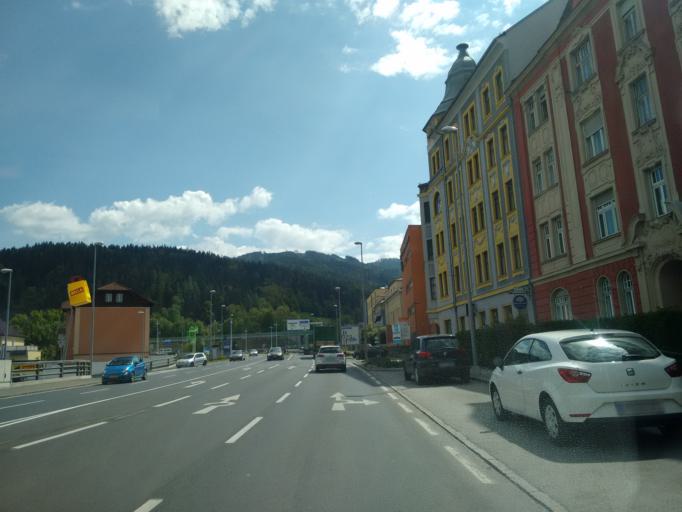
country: AT
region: Styria
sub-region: Politischer Bezirk Bruck-Muerzzuschlag
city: Bruck an der Mur
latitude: 47.4087
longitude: 15.2741
